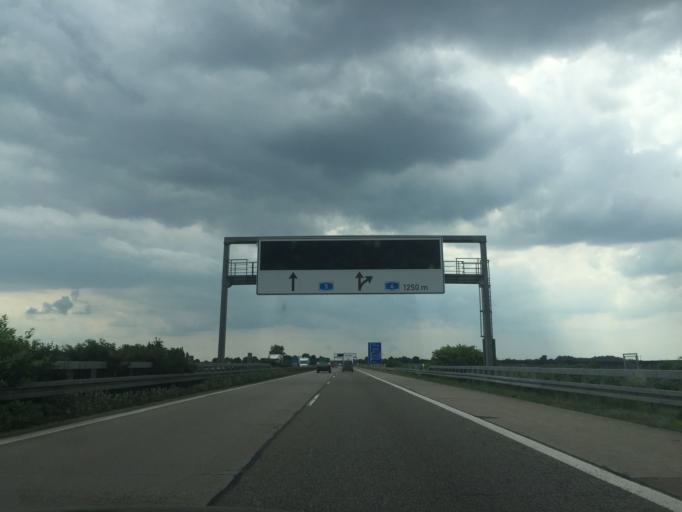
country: DE
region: Baden-Wuerttemberg
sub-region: Karlsruhe Region
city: Walldorf
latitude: 49.2997
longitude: 8.6261
